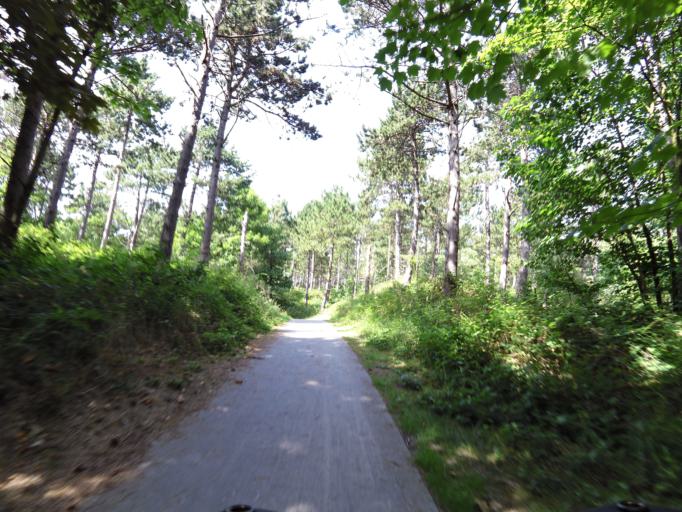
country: NL
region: Zeeland
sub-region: Schouwen-Duiveland
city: Burgh
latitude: 51.6798
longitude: 3.6938
